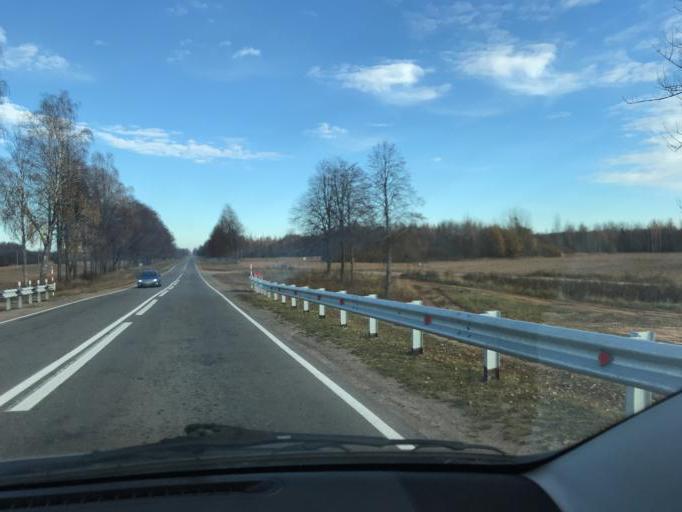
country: BY
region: Vitebsk
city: Haradok
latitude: 55.5035
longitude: 29.9683
